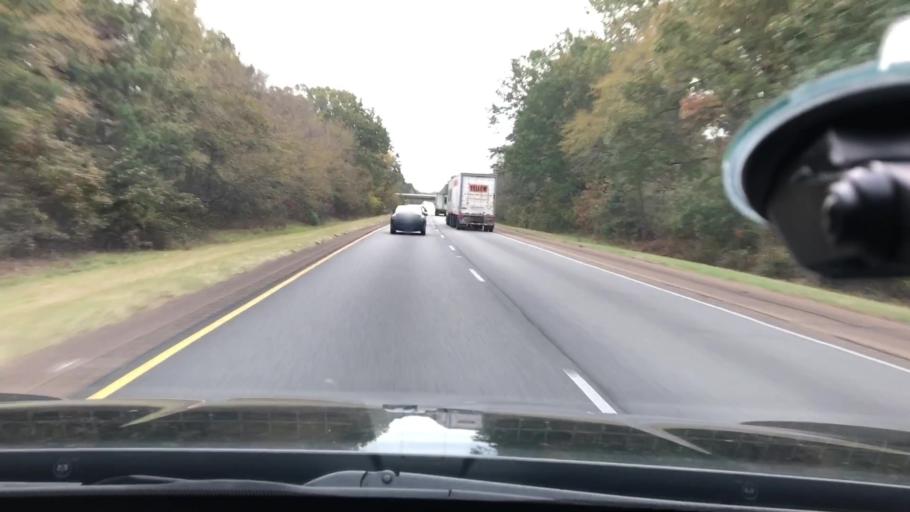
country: US
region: Arkansas
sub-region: Nevada County
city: Prescott
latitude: 33.8468
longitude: -93.3756
